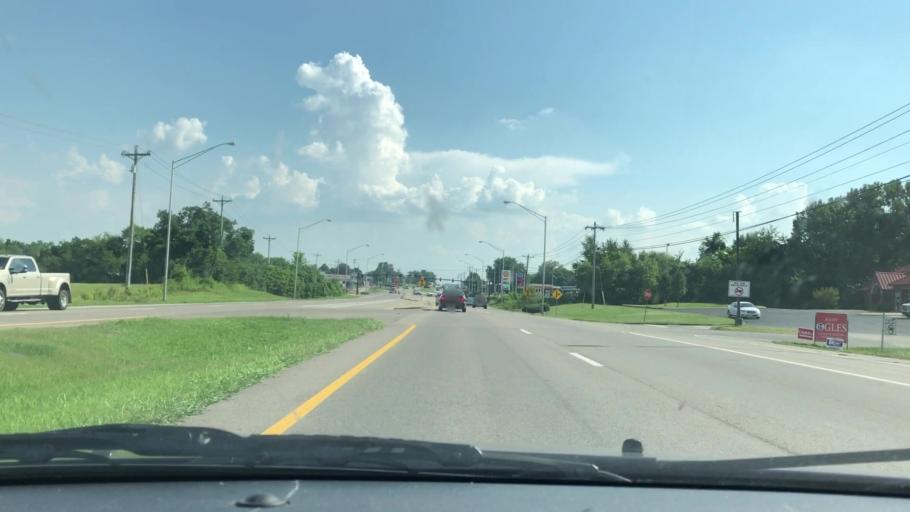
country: US
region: Tennessee
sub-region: Maury County
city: Spring Hill
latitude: 35.7142
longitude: -86.9726
